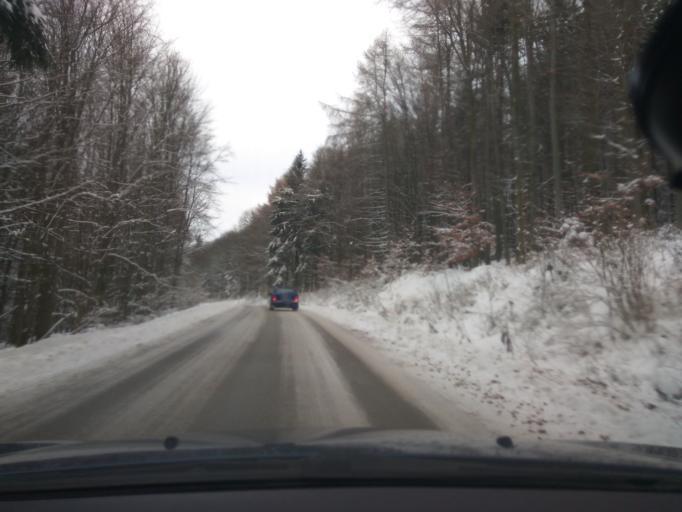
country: CZ
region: Zlin
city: Strani
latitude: 48.8502
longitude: 17.6857
